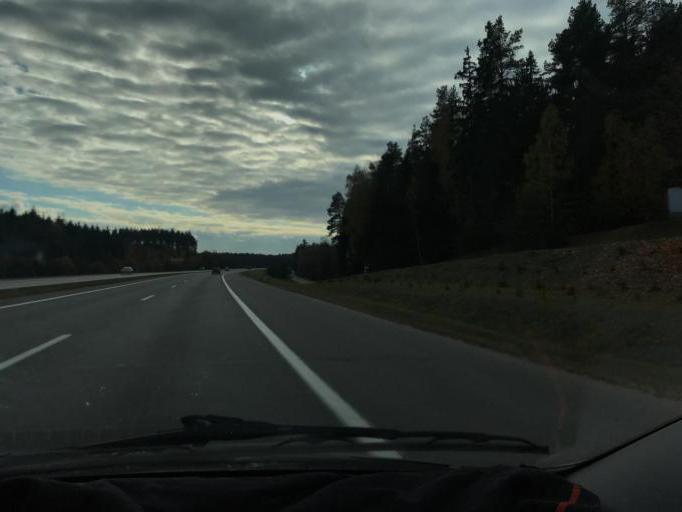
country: BY
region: Minsk
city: Astrashytski Haradok
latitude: 54.0424
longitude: 27.6985
